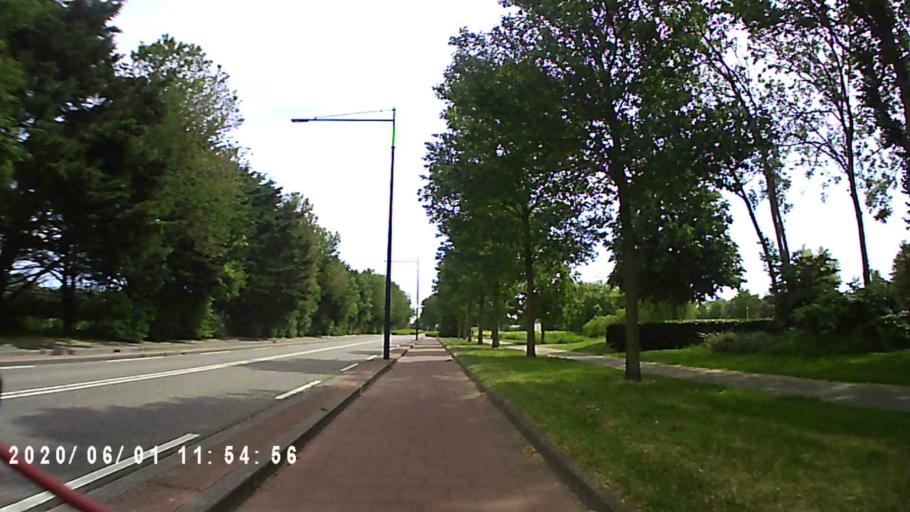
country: NL
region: Friesland
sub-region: Gemeente Harlingen
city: Harlingen
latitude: 53.1633
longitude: 5.4306
